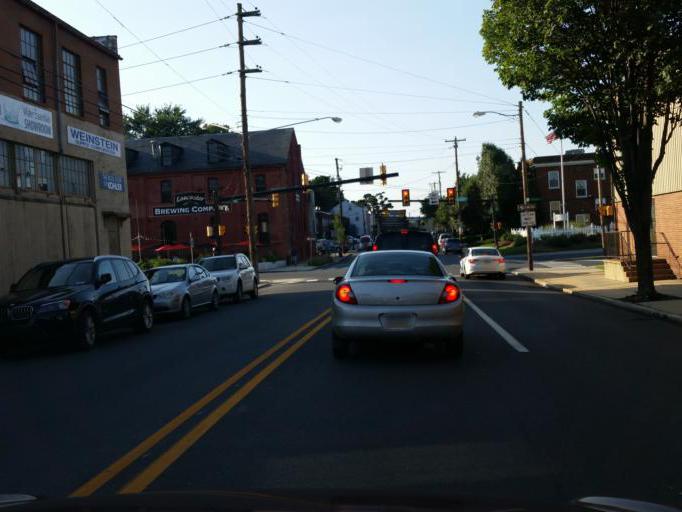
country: US
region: Pennsylvania
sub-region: Lancaster County
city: Lancaster
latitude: 40.0430
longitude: -76.2979
